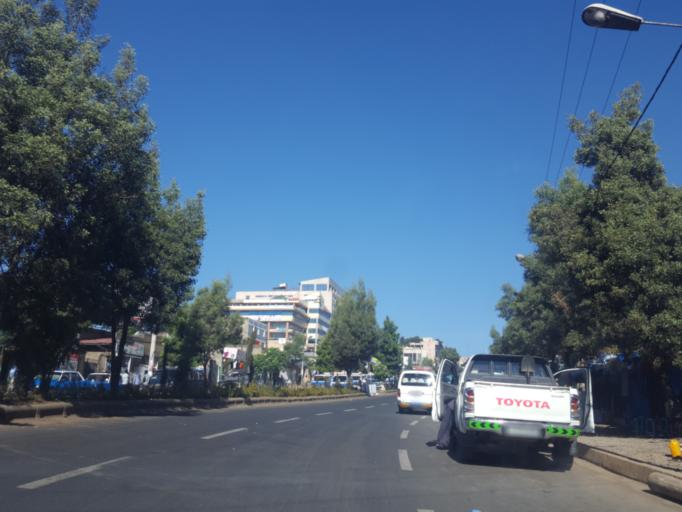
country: ET
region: Adis Abeba
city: Addis Ababa
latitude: 9.0583
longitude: 38.7389
